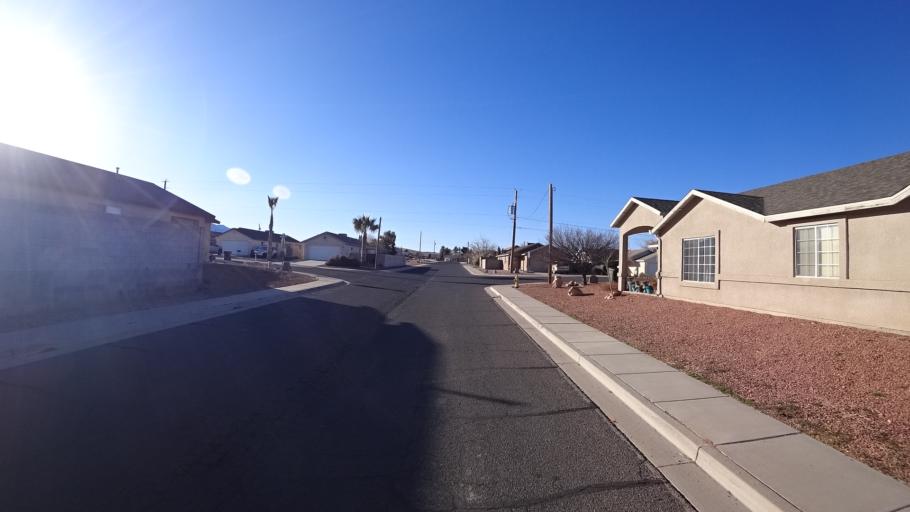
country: US
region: Arizona
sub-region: Mohave County
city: Kingman
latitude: 35.1976
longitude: -114.0158
